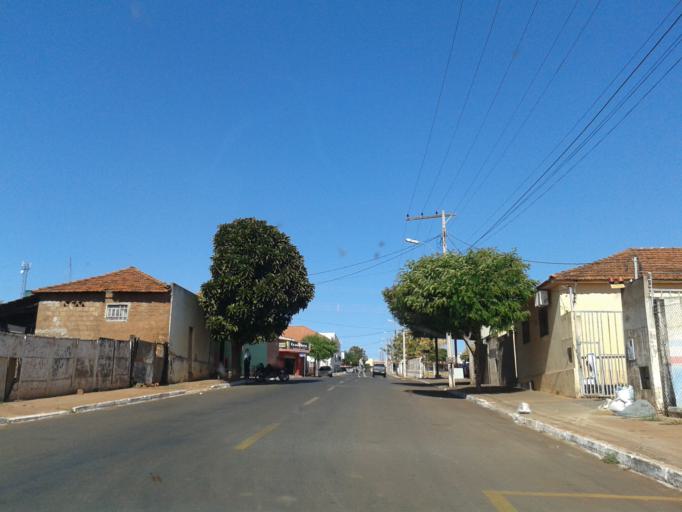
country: BR
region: Minas Gerais
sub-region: Santa Vitoria
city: Santa Vitoria
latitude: -18.8391
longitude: -50.1268
